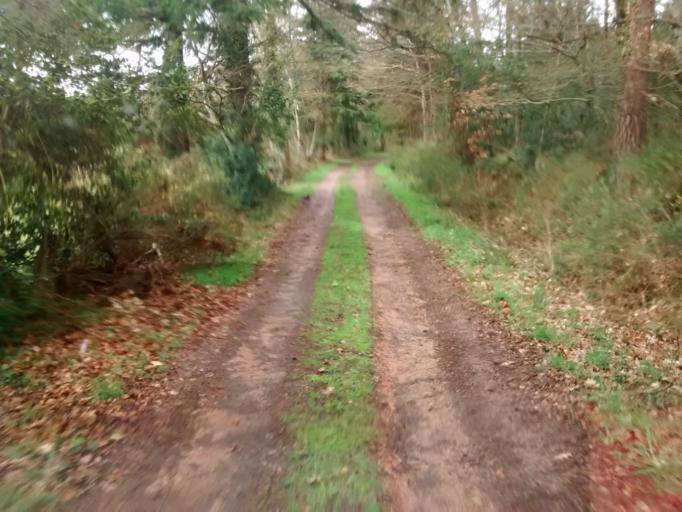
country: FR
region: Brittany
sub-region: Departement du Morbihan
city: Molac
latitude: 47.7225
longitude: -2.4053
